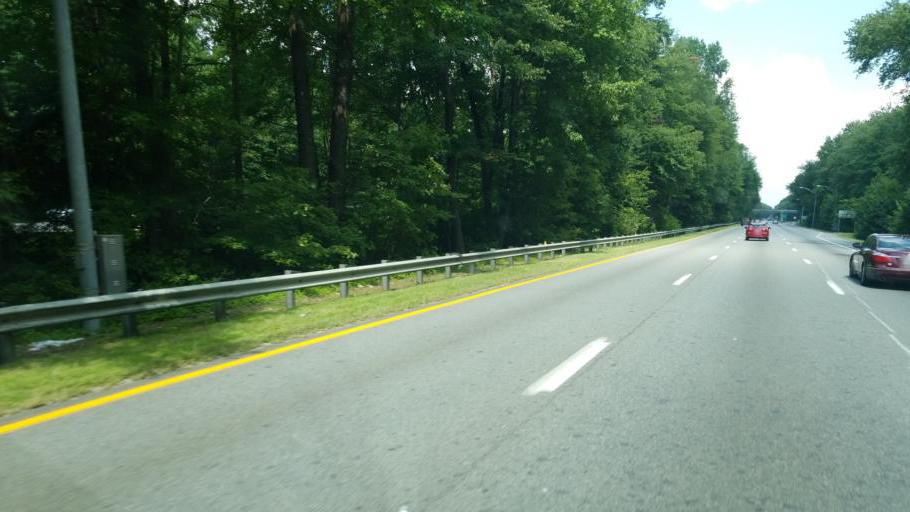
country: US
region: Virginia
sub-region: City of Suffolk
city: Suffolk
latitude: 36.7619
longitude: -76.4907
